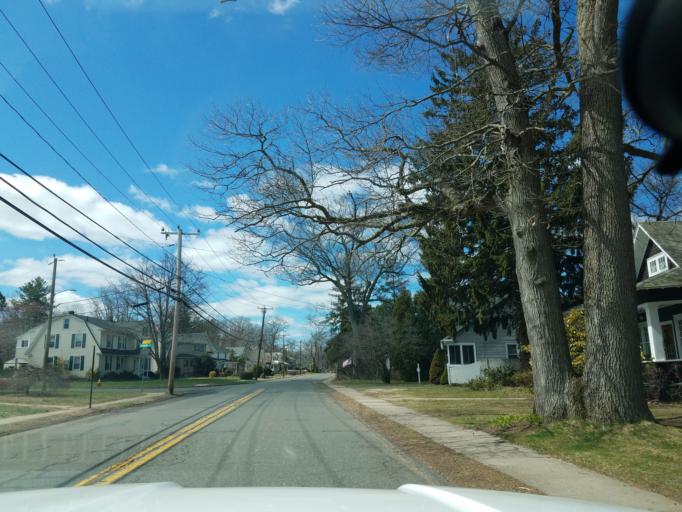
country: US
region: Connecticut
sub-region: Hartford County
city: East Hartford
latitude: 41.7839
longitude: -72.6000
